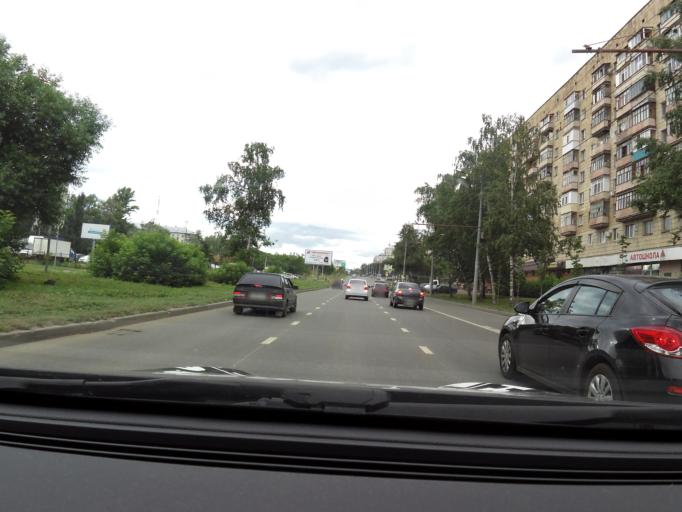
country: RU
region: Tatarstan
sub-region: Gorod Kazan'
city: Kazan
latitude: 55.8207
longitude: 49.0524
